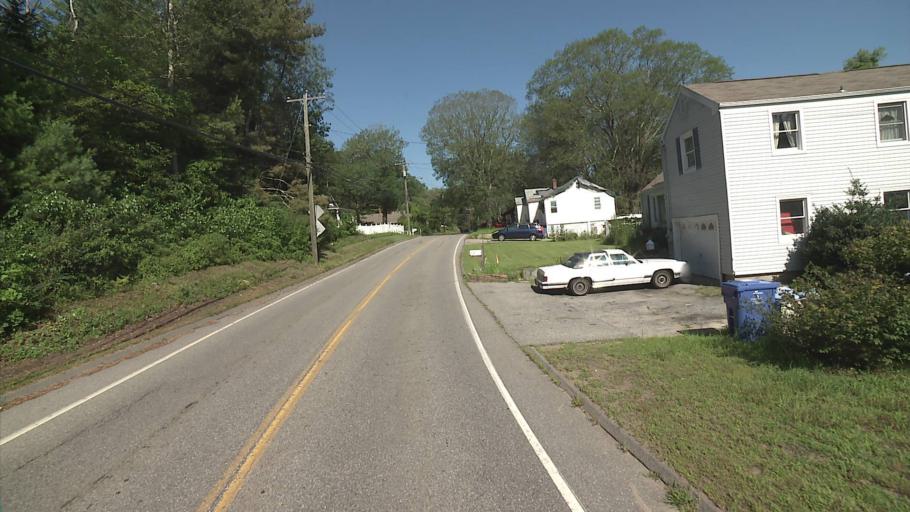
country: US
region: Connecticut
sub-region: New London County
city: Montville Center
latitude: 41.4616
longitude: -72.1527
